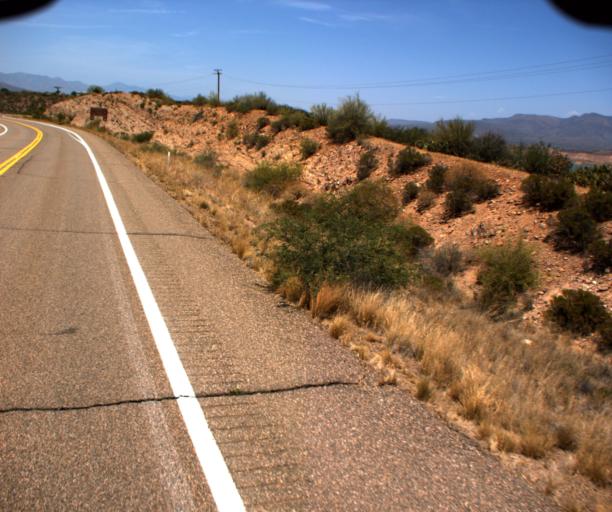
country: US
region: Arizona
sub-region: Gila County
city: Tonto Basin
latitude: 33.6657
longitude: -111.1282
